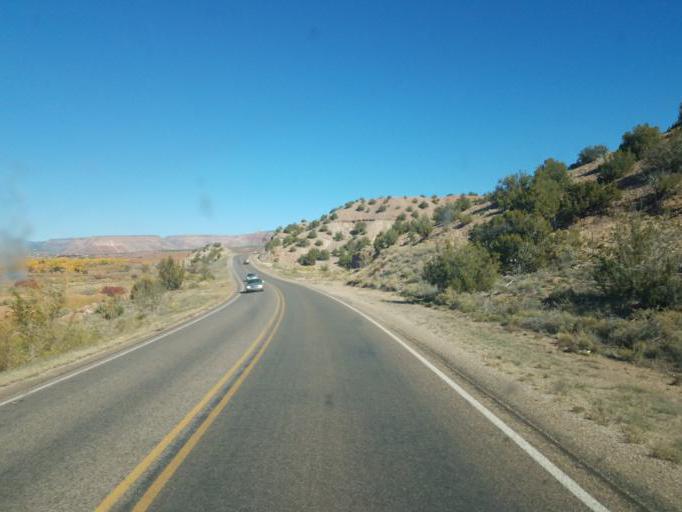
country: US
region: New Mexico
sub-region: Sandoval County
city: Jemez Pueblo
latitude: 35.6296
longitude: -106.7242
